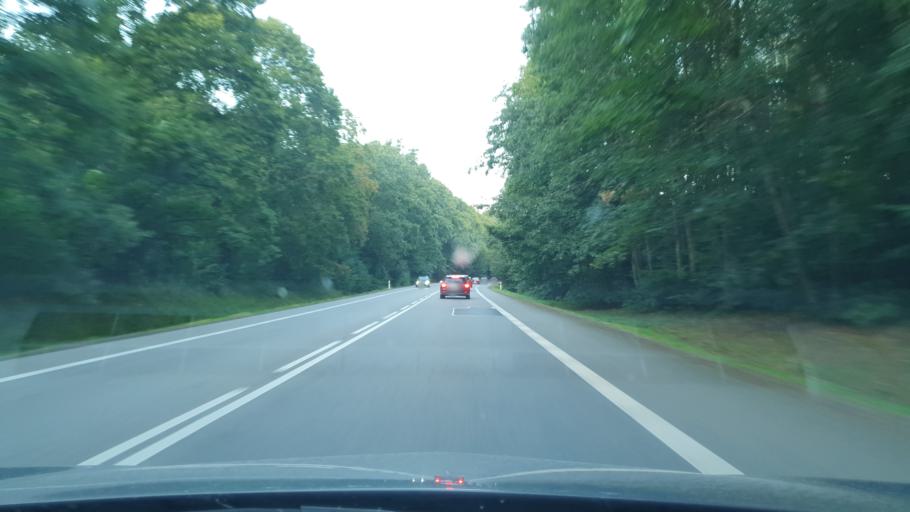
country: PL
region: Pomeranian Voivodeship
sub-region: Powiat slupski
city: Potegowo
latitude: 54.4861
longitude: 17.5725
